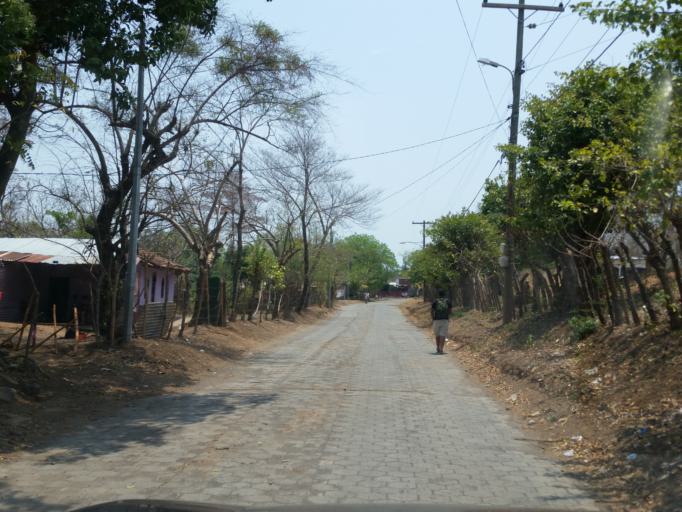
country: NI
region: Granada
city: Granada
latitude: 11.9299
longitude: -85.9705
